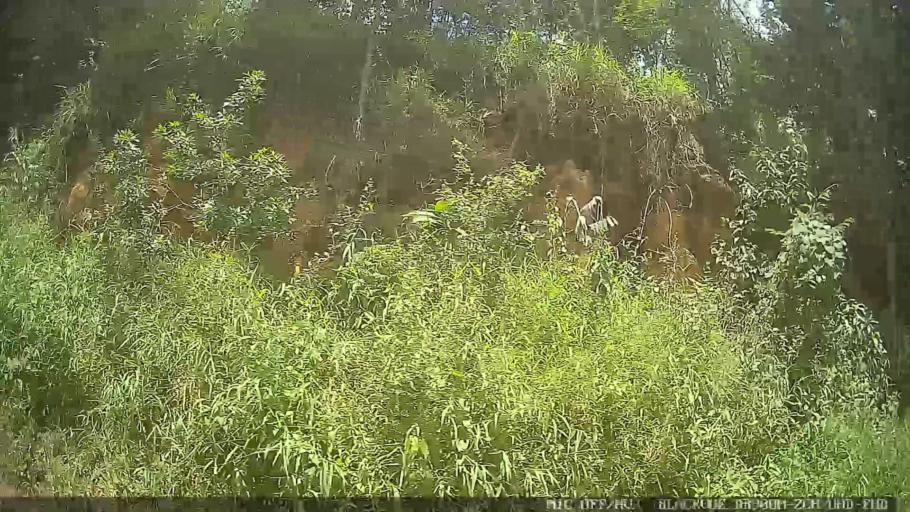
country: BR
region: Minas Gerais
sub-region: Extrema
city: Extrema
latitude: -22.8680
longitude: -46.2878
